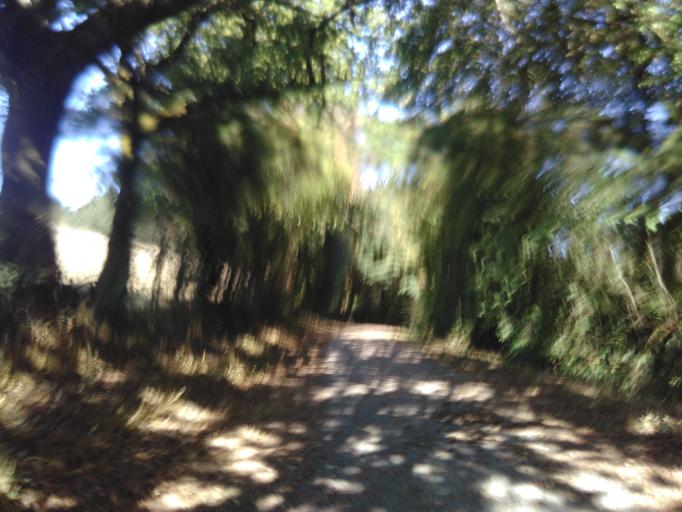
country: FR
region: Pays de la Loire
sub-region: Departement de la Vendee
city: La Chaize-le-Vicomte
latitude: 46.6628
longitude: -1.3032
